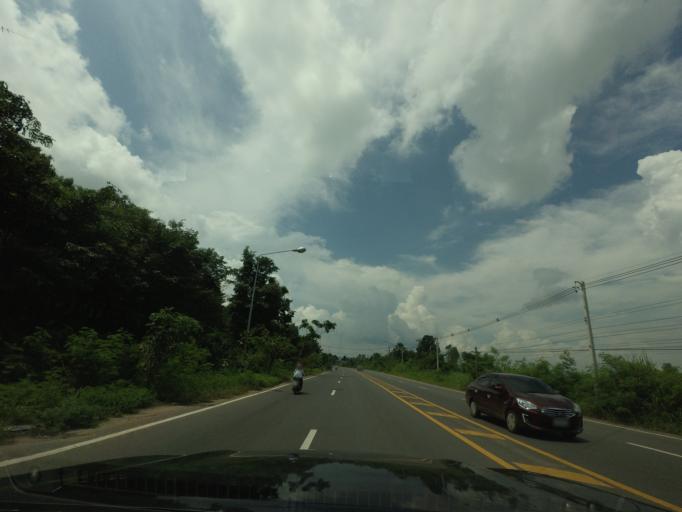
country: TH
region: Khon Kaen
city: Wiang Kao
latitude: 16.6763
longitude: 102.3293
